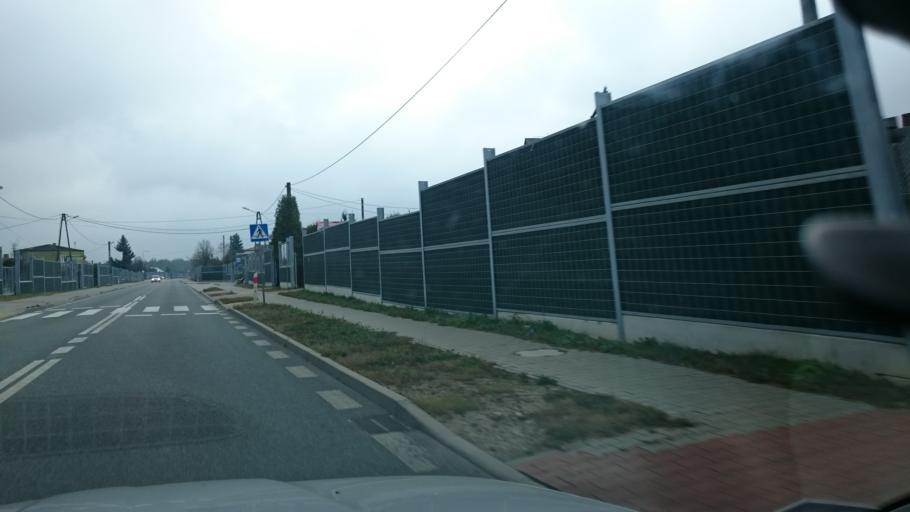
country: PL
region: Swietokrzyskie
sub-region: Powiat konecki
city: Konskie
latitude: 51.1446
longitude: 20.3633
